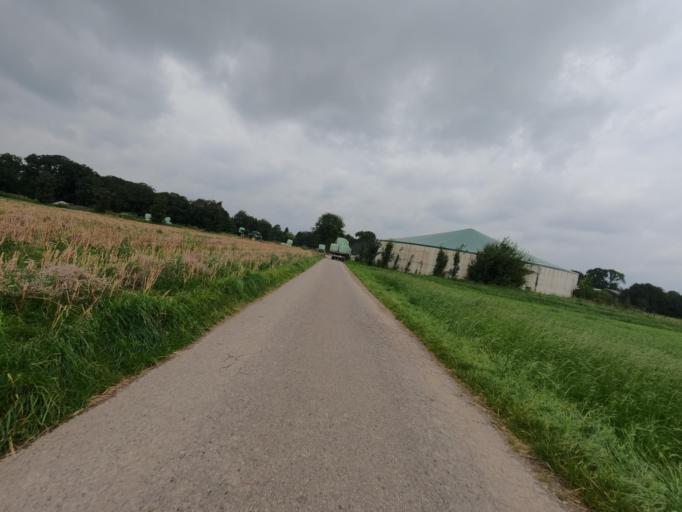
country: DE
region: North Rhine-Westphalia
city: Baesweiler
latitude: 50.9464
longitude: 6.1652
